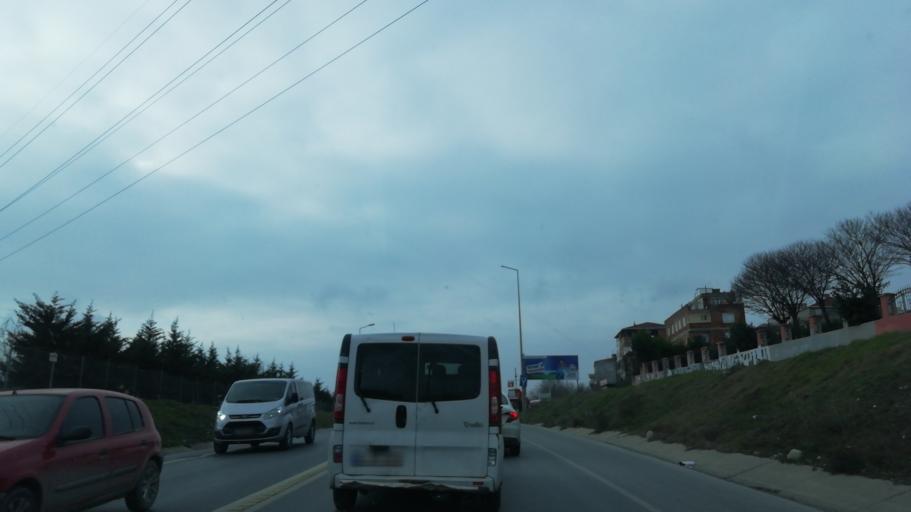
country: TR
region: Istanbul
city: Esenyurt
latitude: 41.0555
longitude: 28.7253
